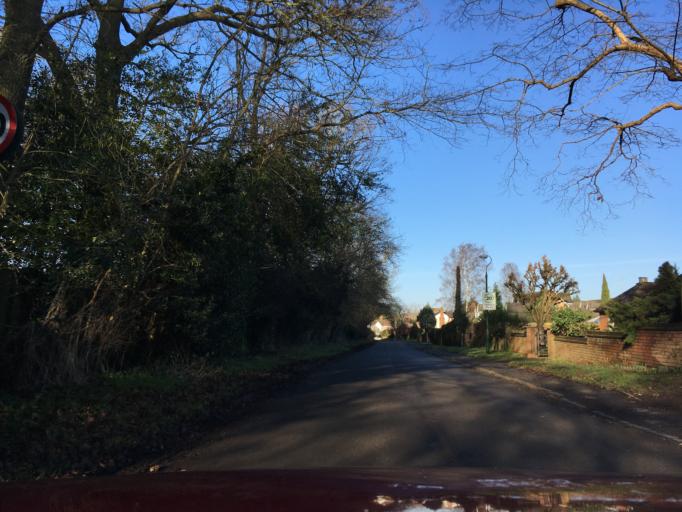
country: GB
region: England
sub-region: Warwickshire
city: Stratford-upon-Avon
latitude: 52.2045
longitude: -1.6564
